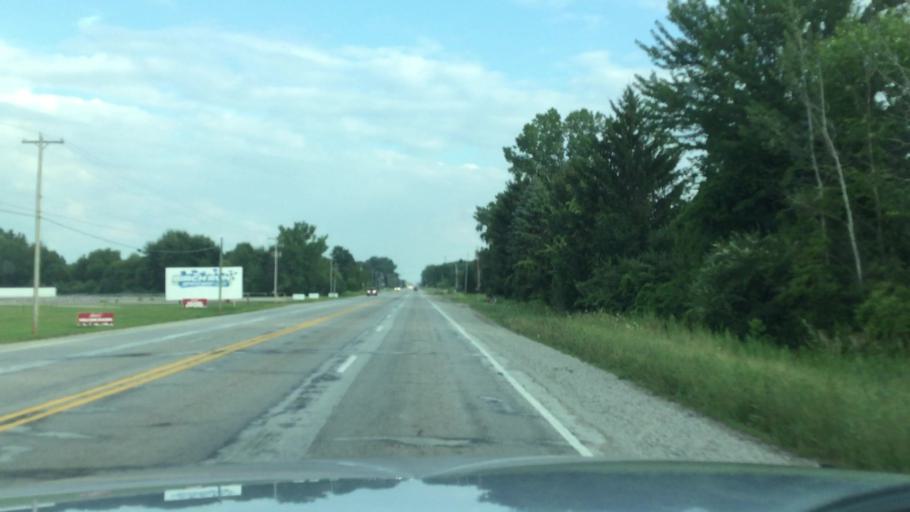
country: US
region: Michigan
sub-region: Saginaw County
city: Birch Run
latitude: 43.2675
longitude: -83.7824
